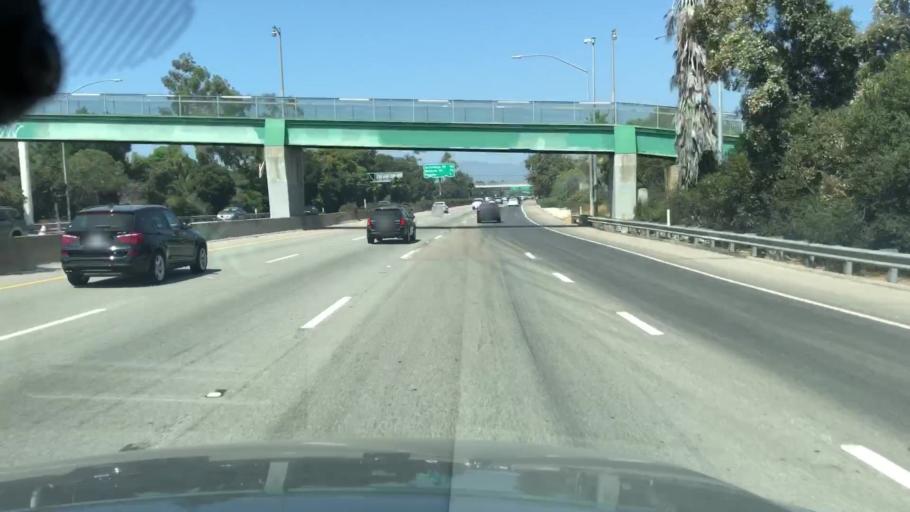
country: US
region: California
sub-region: Santa Barbara County
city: Santa Barbara
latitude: 34.4179
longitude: -119.7096
